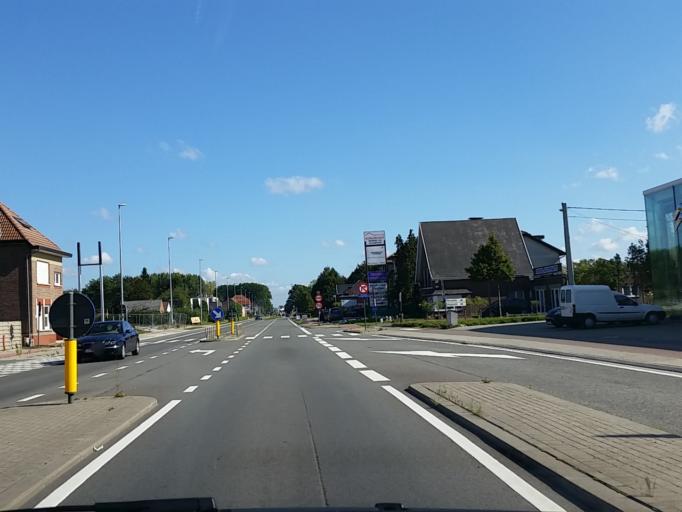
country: BE
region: Flanders
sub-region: Provincie Vlaams-Brabant
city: Kampenhout
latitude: 50.9488
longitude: 4.5784
